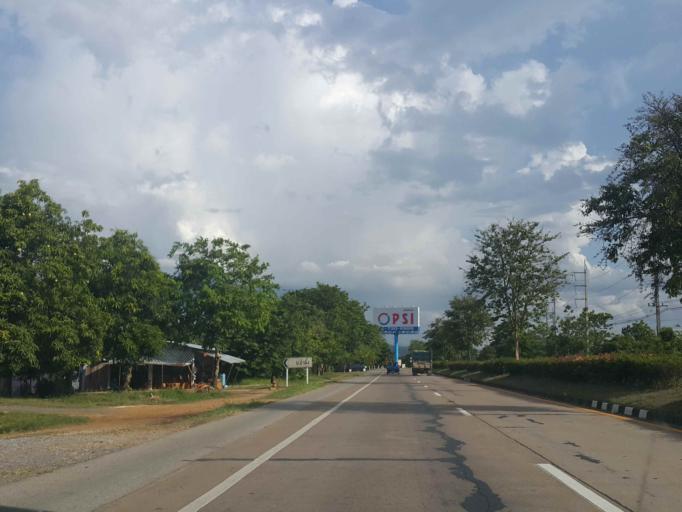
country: TH
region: Phrae
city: Sung Men
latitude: 18.0271
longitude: 100.1111
